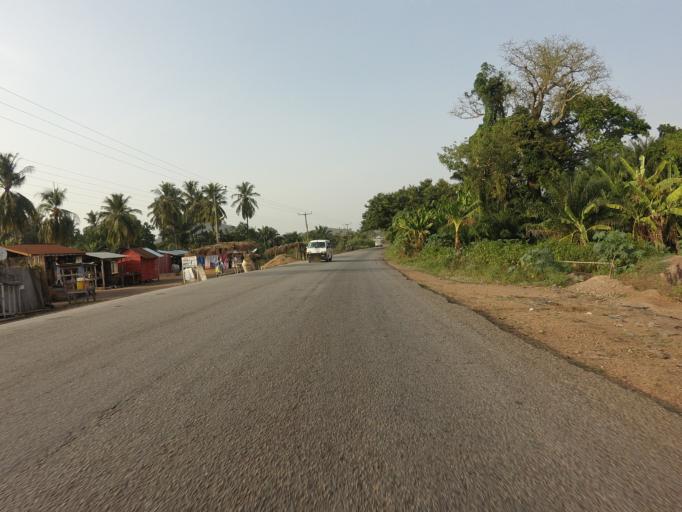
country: GH
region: Volta
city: Ho
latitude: 6.4089
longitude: 0.1726
